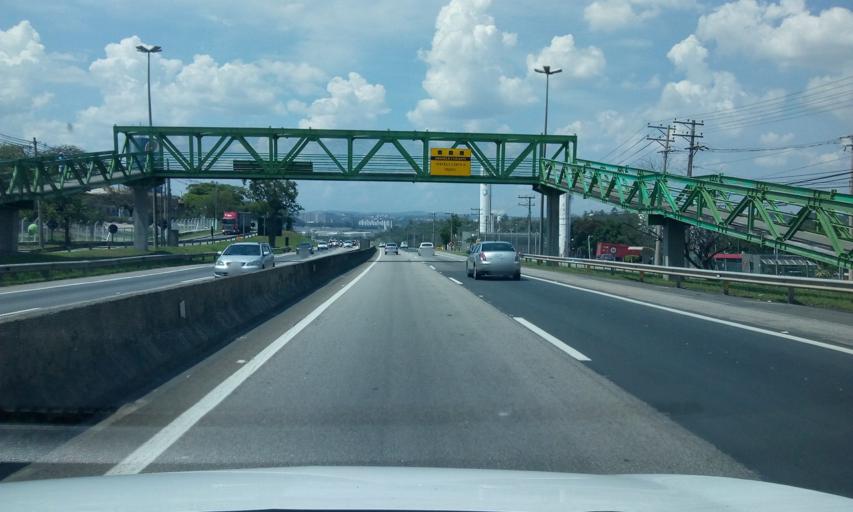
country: BR
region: Sao Paulo
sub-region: Jundiai
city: Jundiai
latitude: -23.1796
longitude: -46.9594
